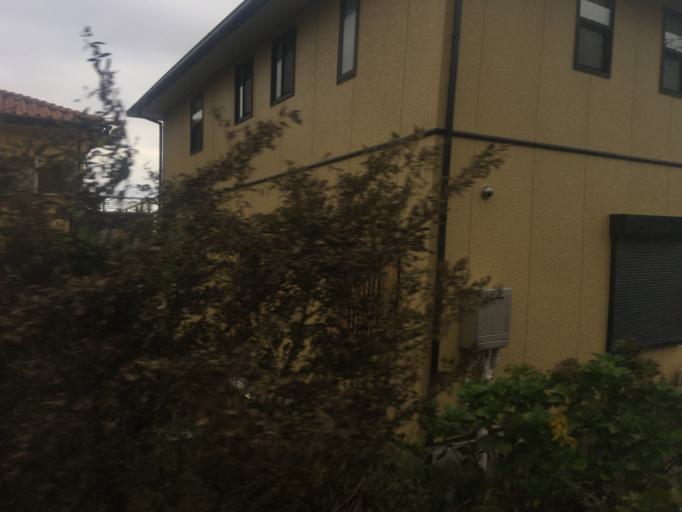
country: JP
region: Chiba
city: Kawaguchi
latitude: 35.1241
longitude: 140.1501
